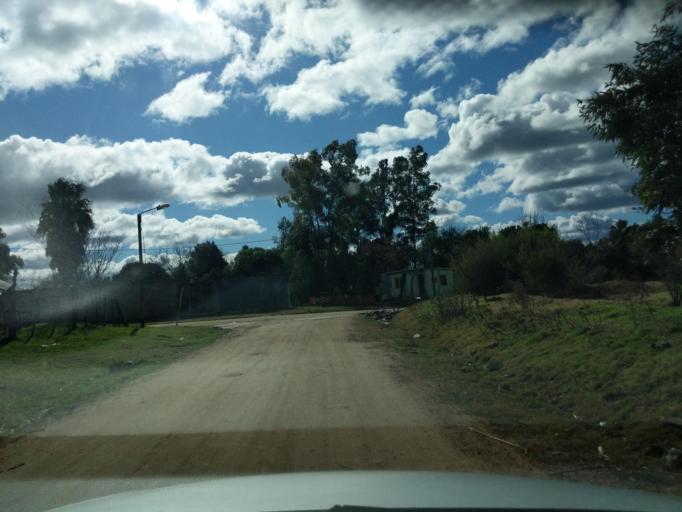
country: UY
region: Florida
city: Florida
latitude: -34.0956
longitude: -56.2325
